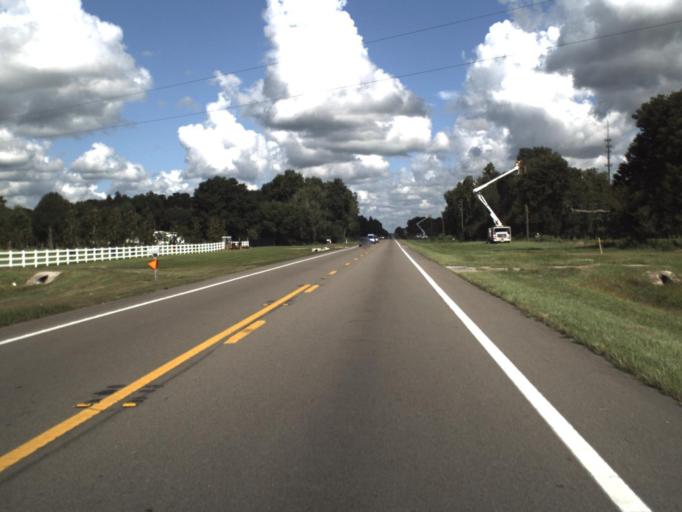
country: US
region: Florida
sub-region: Polk County
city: Kathleen
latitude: 28.2064
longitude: -82.0092
